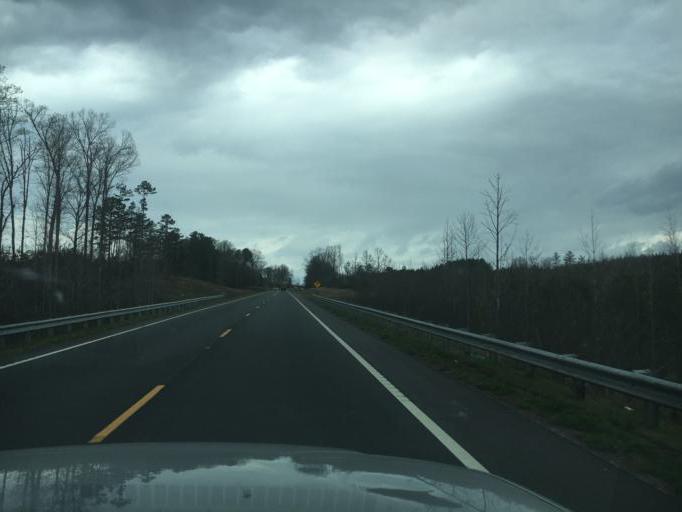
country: US
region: South Carolina
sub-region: Oconee County
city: Walhalla
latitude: 34.7958
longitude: -83.0268
